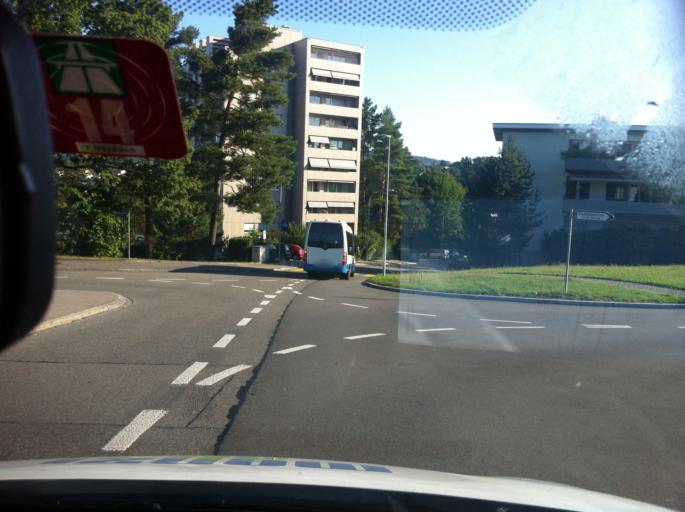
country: CH
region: Zurich
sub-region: Bezirk Meilen
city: Zollikerberg
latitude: 47.3485
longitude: 8.5960
